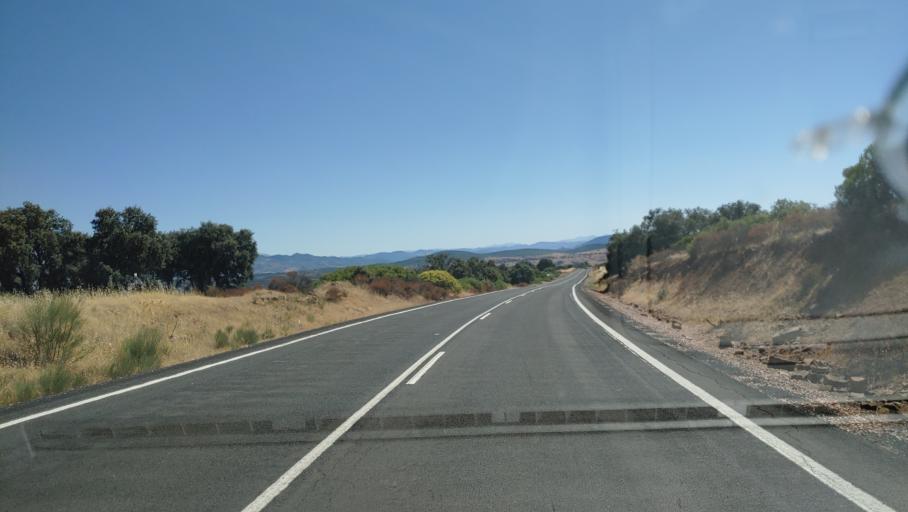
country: ES
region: Castille-La Mancha
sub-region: Provincia de Ciudad Real
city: Albaladejo
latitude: 38.5366
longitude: -2.7858
